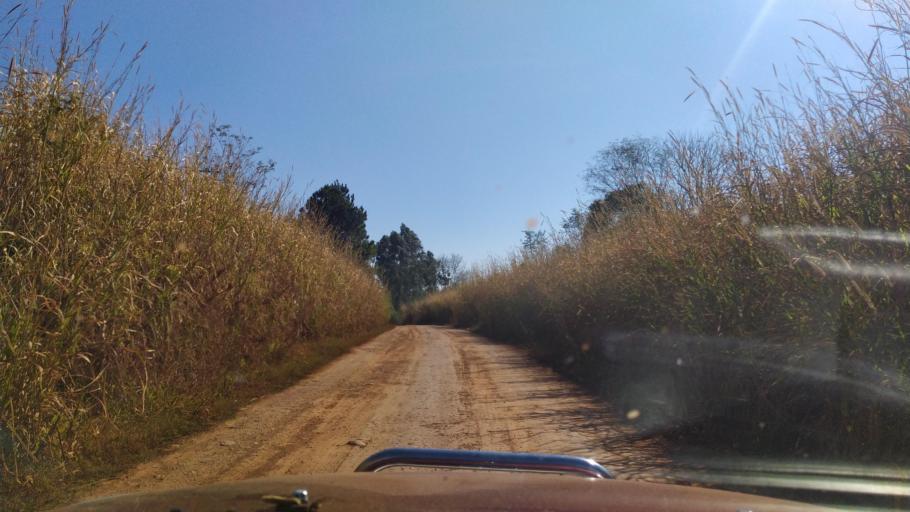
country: AR
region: Misiones
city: El Alcazar
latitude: -26.7169
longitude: -54.6957
